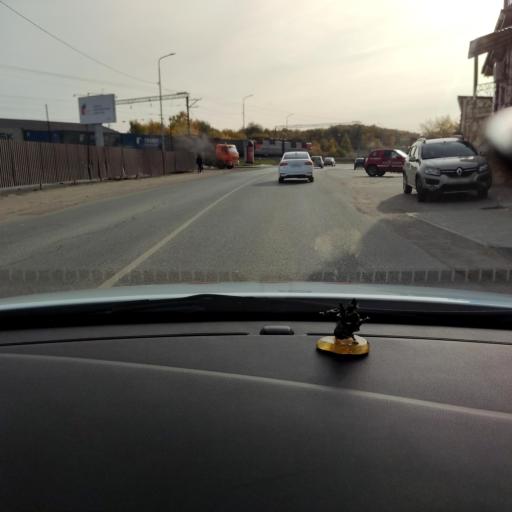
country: RU
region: Tatarstan
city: Vysokaya Gora
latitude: 55.9312
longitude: 49.3051
